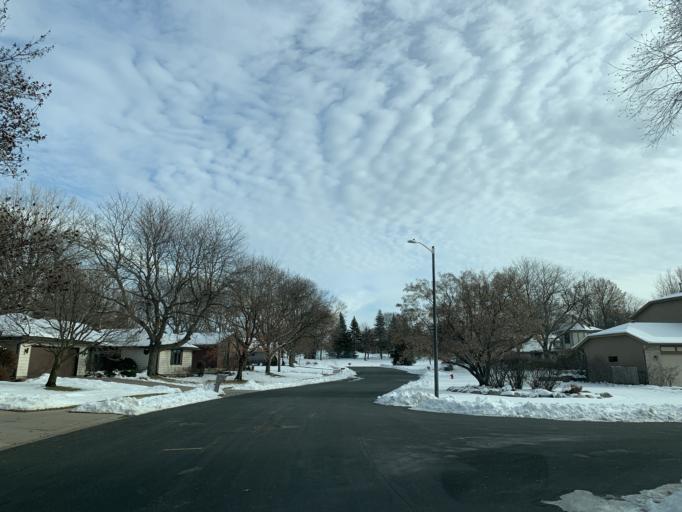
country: US
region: Minnesota
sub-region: Scott County
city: Savage
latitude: 44.8255
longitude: -93.3564
